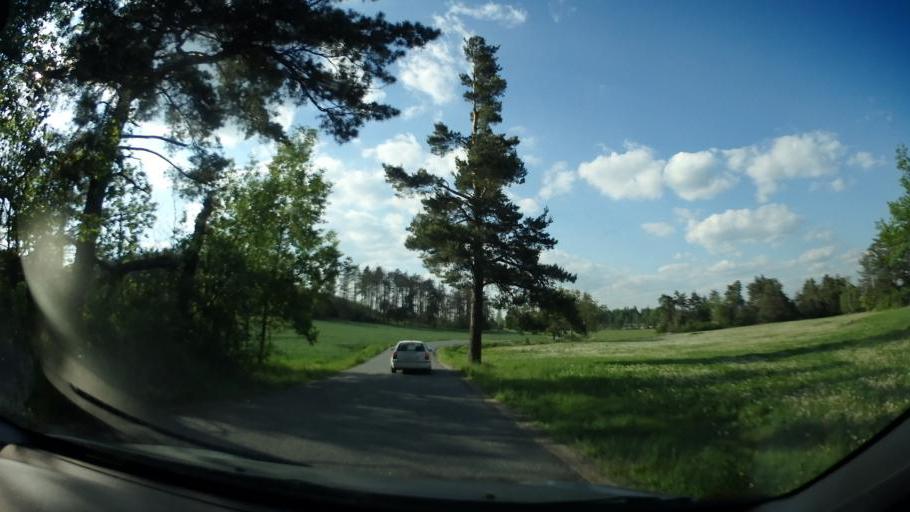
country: CZ
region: Vysocina
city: Budisov
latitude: 49.3069
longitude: 15.9780
